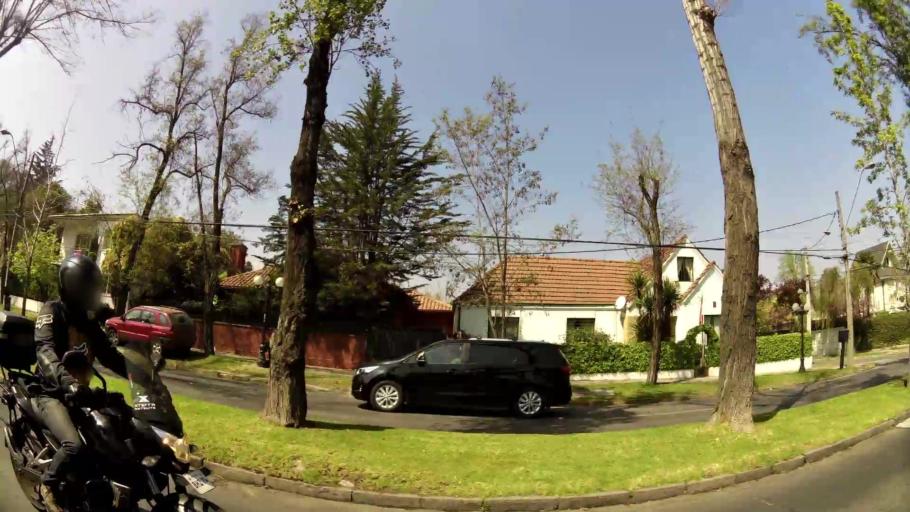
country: CL
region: Santiago Metropolitan
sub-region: Provincia de Santiago
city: Villa Presidente Frei, Nunoa, Santiago, Chile
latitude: -33.4387
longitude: -70.5924
